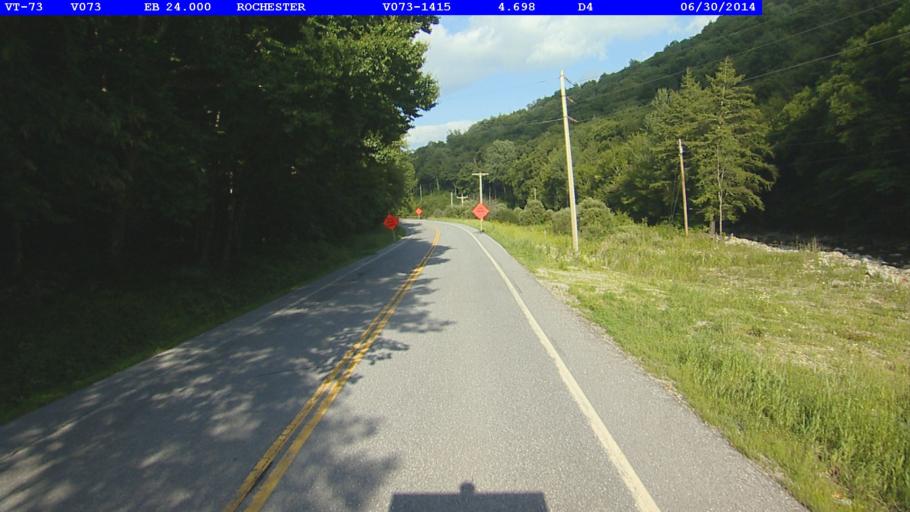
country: US
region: Vermont
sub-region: Rutland County
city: Brandon
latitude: 43.8572
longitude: -72.8784
